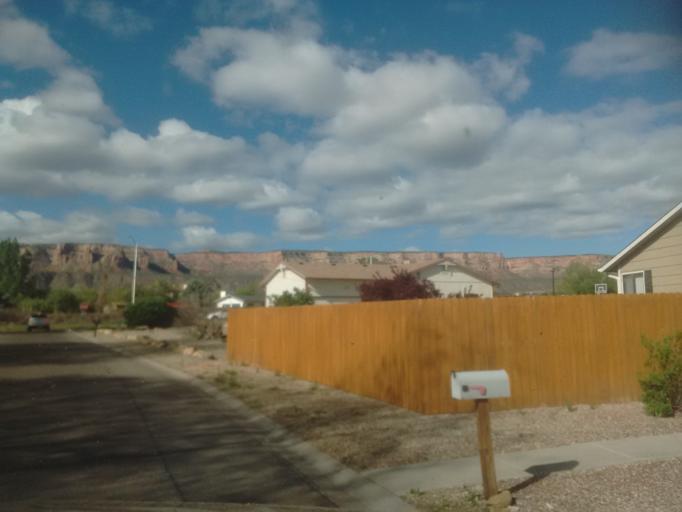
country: US
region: Colorado
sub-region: Mesa County
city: Redlands
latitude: 39.0920
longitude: -108.6550
